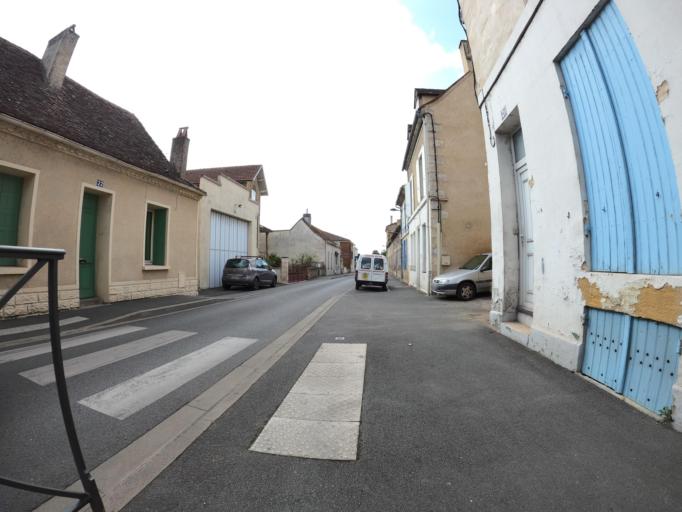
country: FR
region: Aquitaine
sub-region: Departement de la Dordogne
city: Bergerac
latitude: 44.8458
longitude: 0.4813
